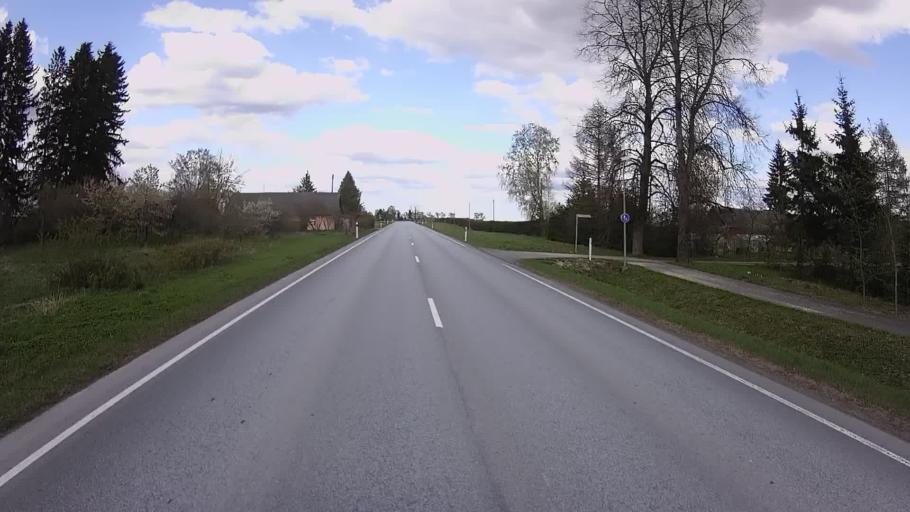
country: EE
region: Jogevamaa
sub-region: Jogeva linn
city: Jogeva
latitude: 58.8069
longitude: 26.5254
